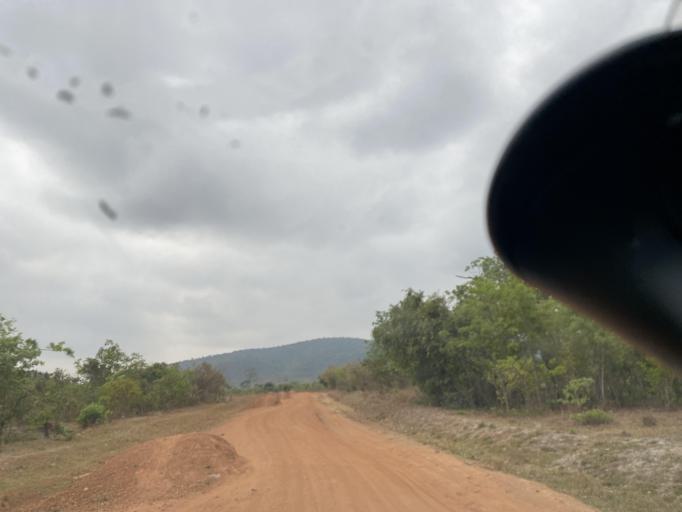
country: ZM
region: Lusaka
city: Chongwe
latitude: -15.1974
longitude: 28.7653
